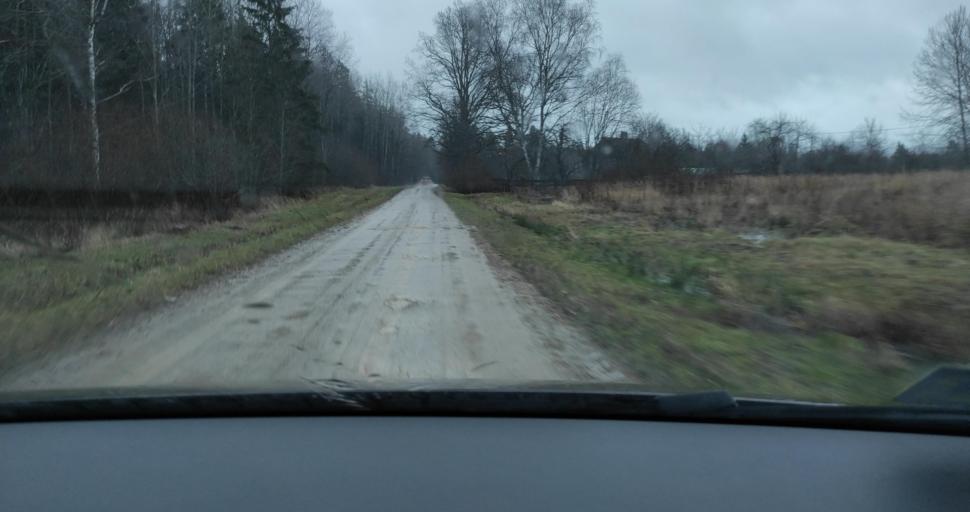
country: LV
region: Skrunda
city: Skrunda
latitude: 56.6079
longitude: 22.1488
